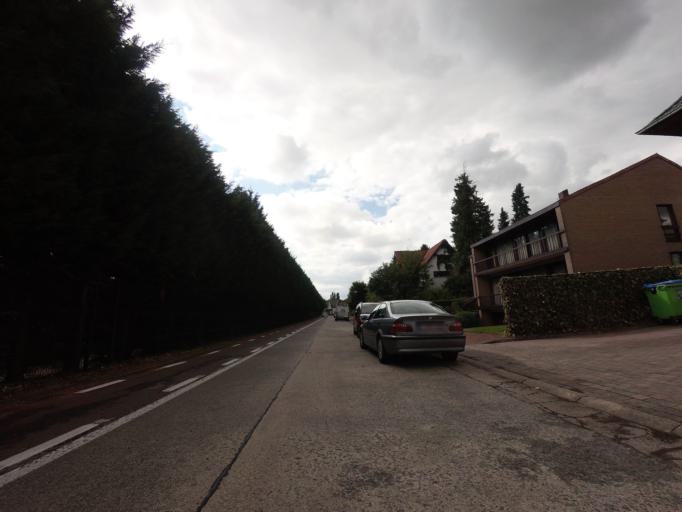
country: BE
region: Flanders
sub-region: Provincie Vlaams-Brabant
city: Meise
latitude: 50.9344
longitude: 4.3366
